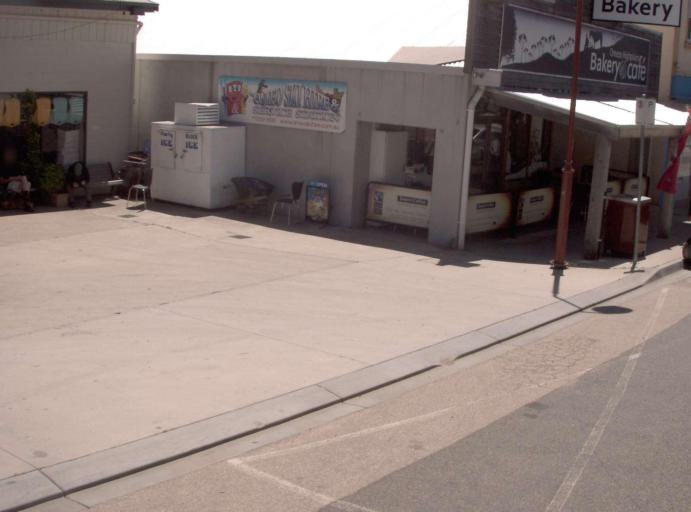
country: AU
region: Victoria
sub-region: Alpine
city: Mount Beauty
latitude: -37.1007
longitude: 147.5905
